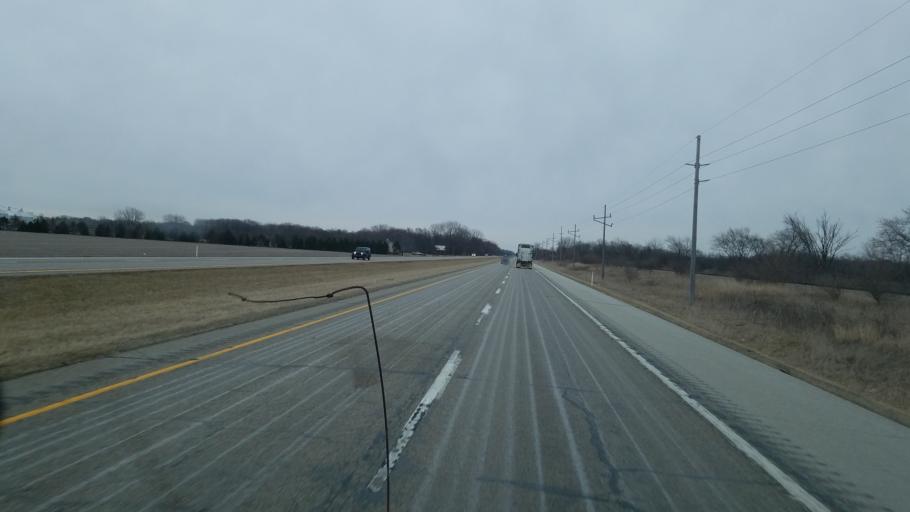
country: US
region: Indiana
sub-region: LaPorte County
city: Kingsford Heights
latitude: 41.4018
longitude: -86.7119
